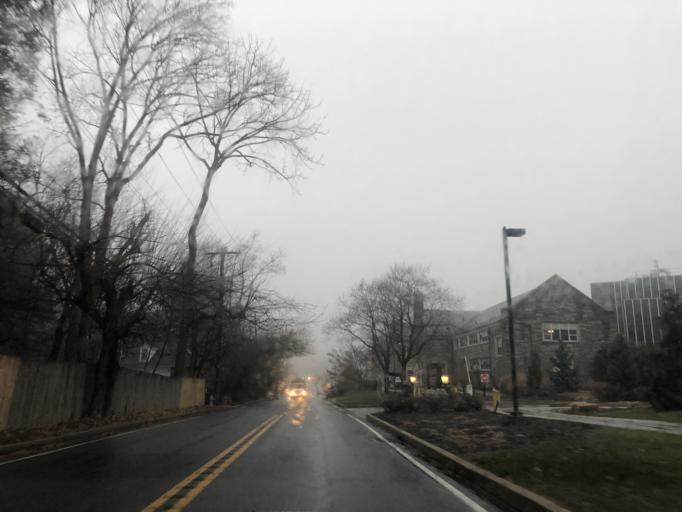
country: US
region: Pennsylvania
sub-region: Delaware County
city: Radnor
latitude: 40.0375
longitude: -75.3455
